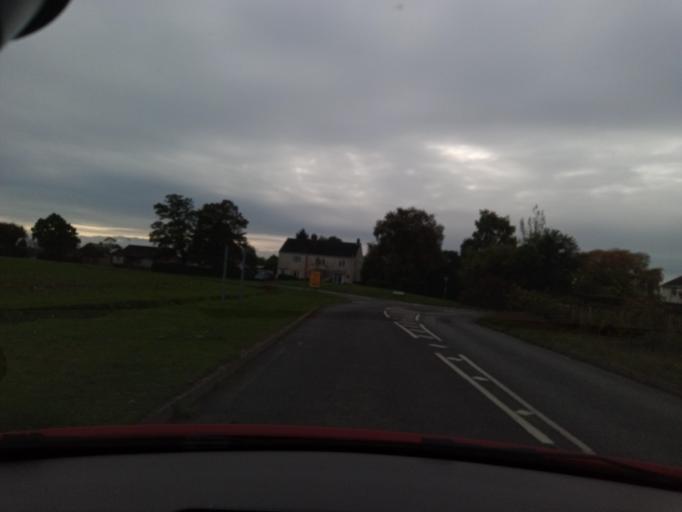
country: GB
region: England
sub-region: Essex
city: West Mersea
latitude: 51.7851
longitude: 0.9398
